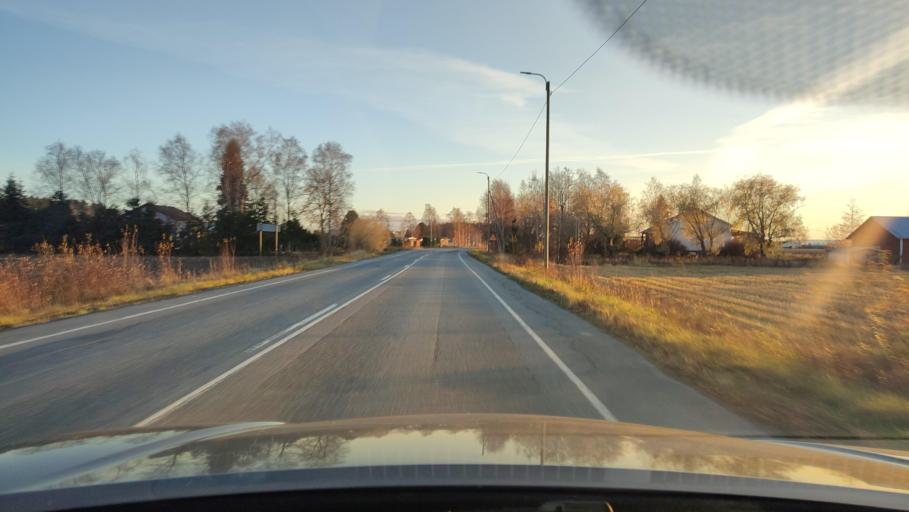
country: FI
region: Ostrobothnia
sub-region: Sydosterbotten
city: Naerpes
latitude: 62.4523
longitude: 21.3530
